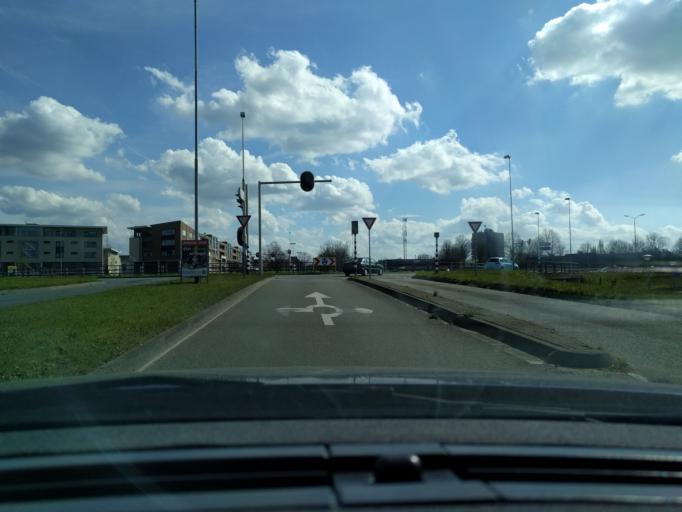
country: NL
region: North Brabant
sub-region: Gemeente Veldhoven
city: Veldhoven
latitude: 51.4251
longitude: 5.4035
